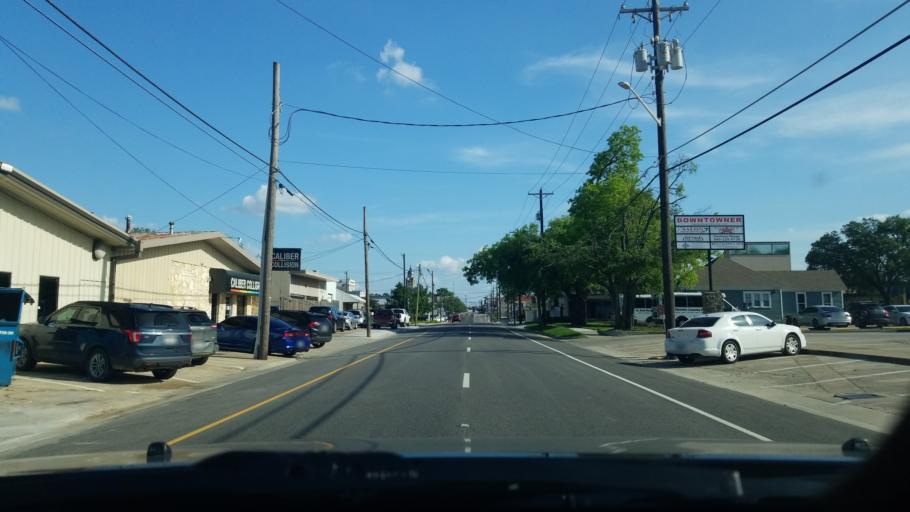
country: US
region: Texas
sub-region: Denton County
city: Denton
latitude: 33.2210
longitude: -97.1336
